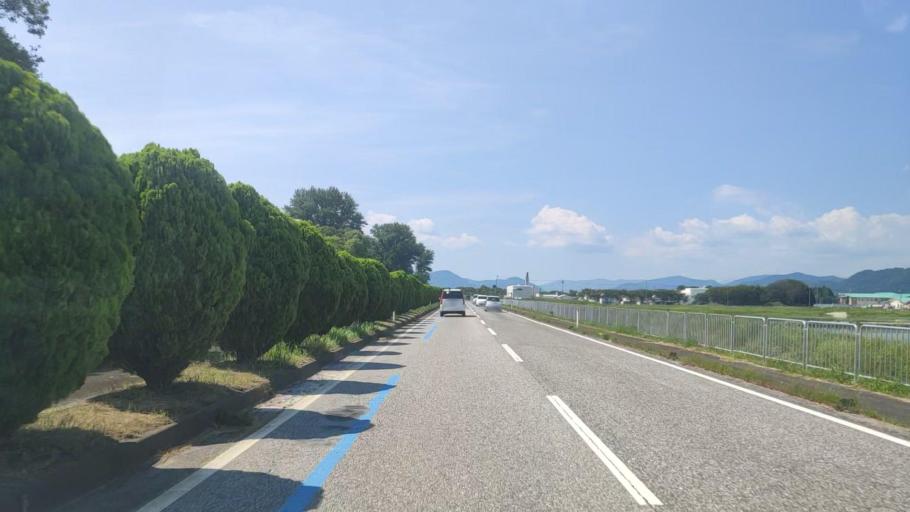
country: JP
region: Shiga Prefecture
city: Nagahama
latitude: 35.4221
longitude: 136.1988
